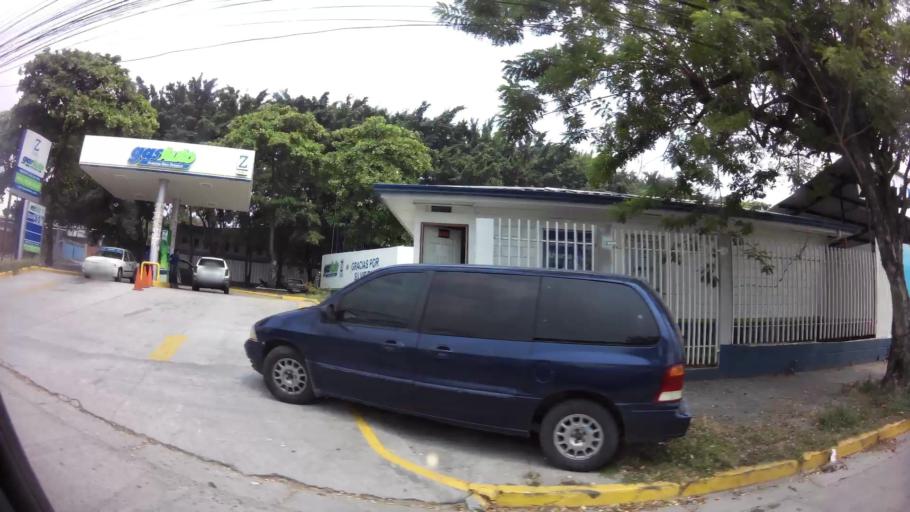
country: HN
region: Cortes
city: San Pedro Sula
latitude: 15.4861
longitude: -88.0290
